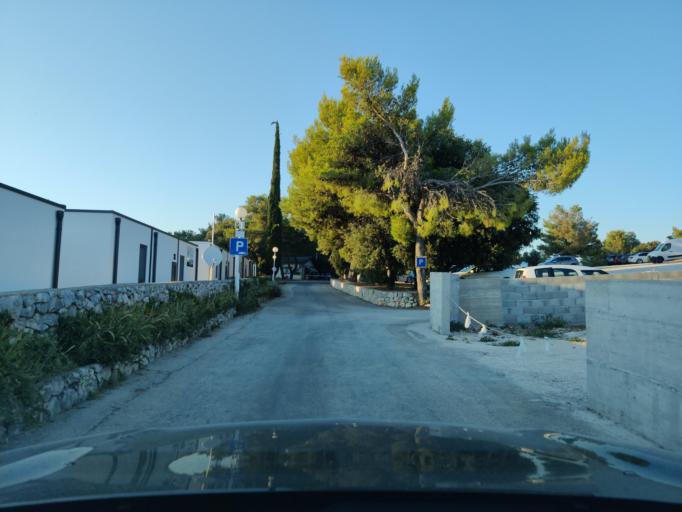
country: HR
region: Sibensko-Kniniska
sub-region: Grad Sibenik
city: Tisno
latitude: 43.8083
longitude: 15.6282
